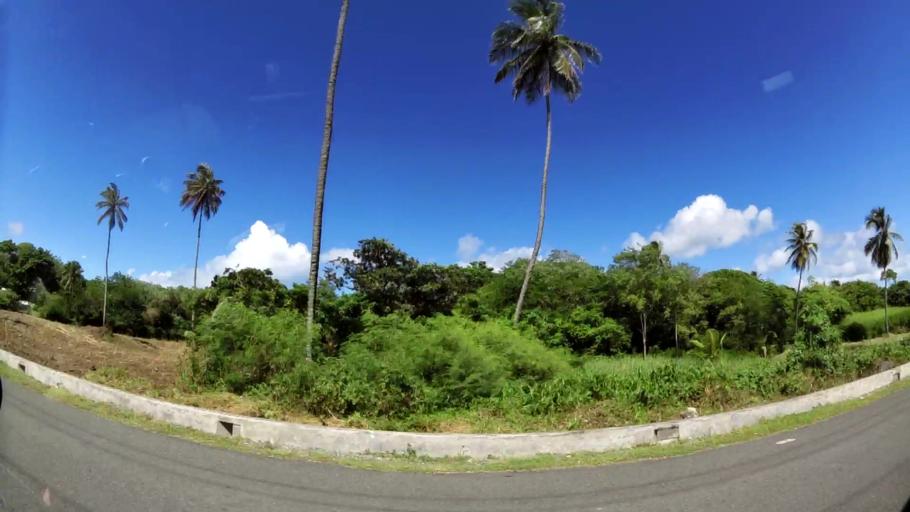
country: TT
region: Tobago
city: Scarborough
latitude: 11.1573
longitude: -60.7723
